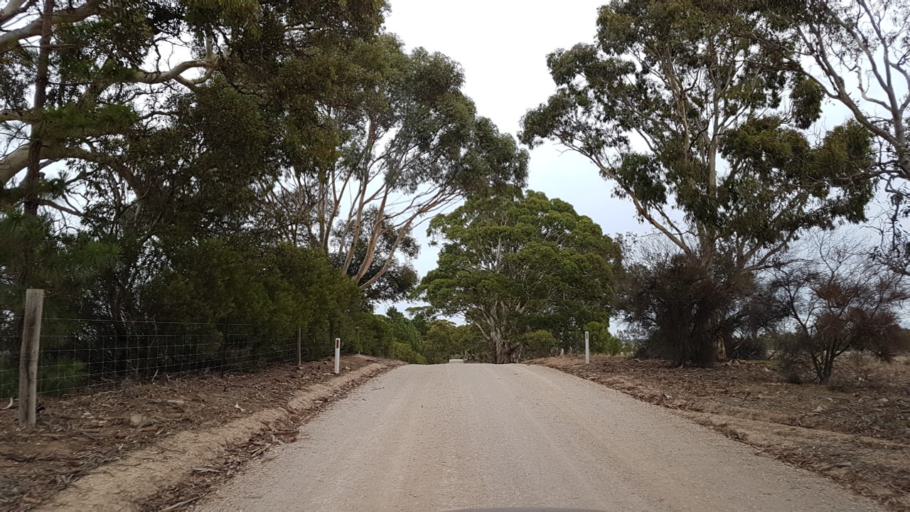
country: AU
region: South Australia
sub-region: Mount Barker
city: Nairne
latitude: -35.0009
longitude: 139.0174
